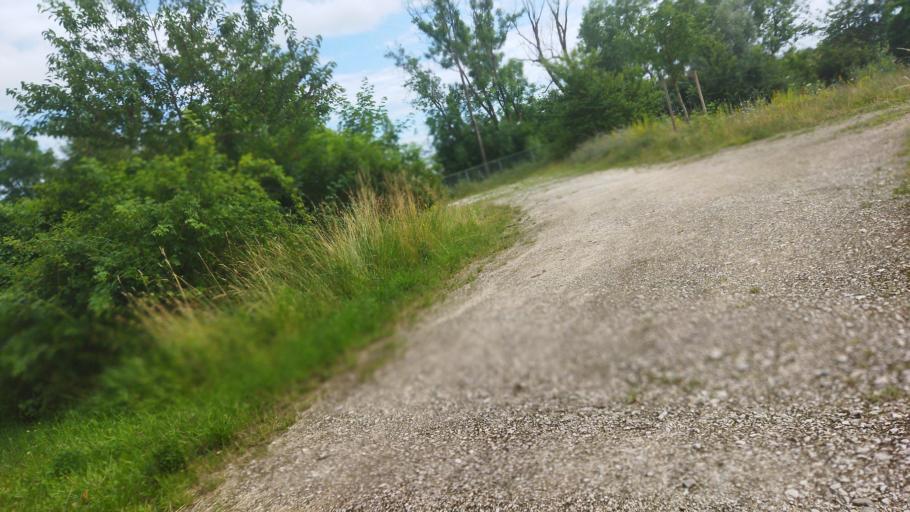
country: DE
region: Bavaria
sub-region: Upper Palatinate
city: Tegernheim
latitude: 49.0073
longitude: 12.1717
